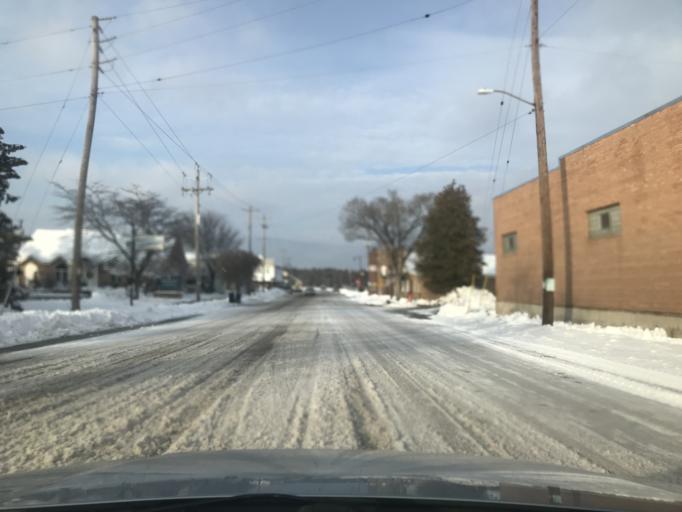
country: US
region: Wisconsin
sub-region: Marinette County
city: Peshtigo
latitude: 45.0531
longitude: -87.7491
